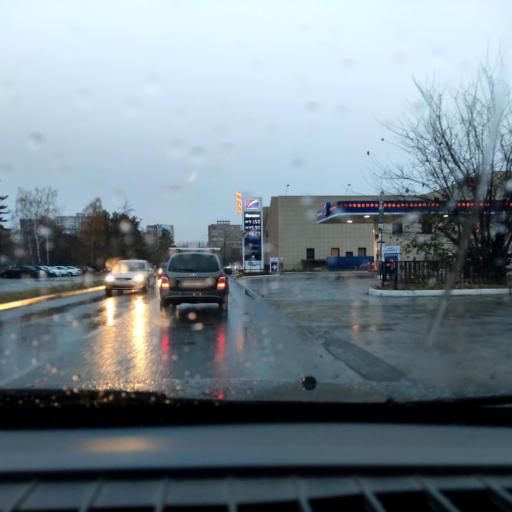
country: RU
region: Samara
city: Tol'yatti
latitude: 53.5238
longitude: 49.3293
